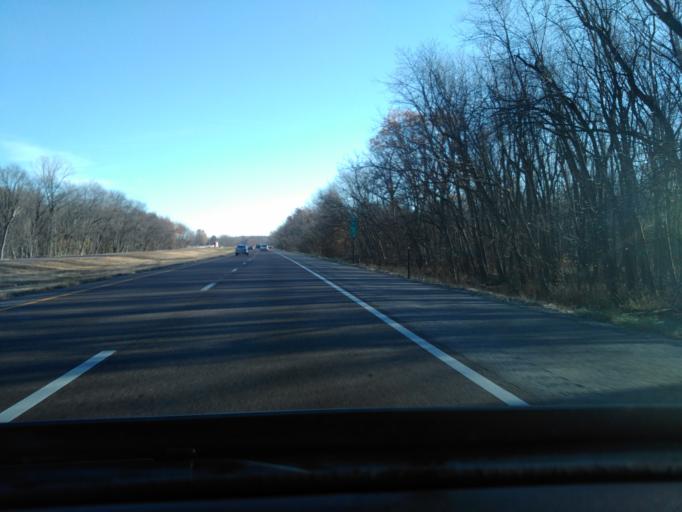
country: US
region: Illinois
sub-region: Madison County
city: Troy
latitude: 38.7583
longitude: -89.8394
